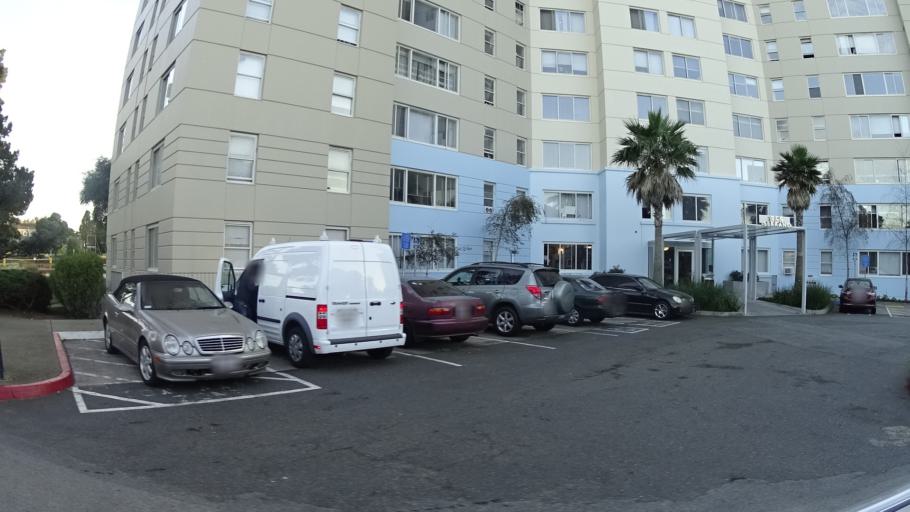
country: US
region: California
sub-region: San Mateo County
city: Daly City
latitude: 37.7190
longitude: -122.4807
